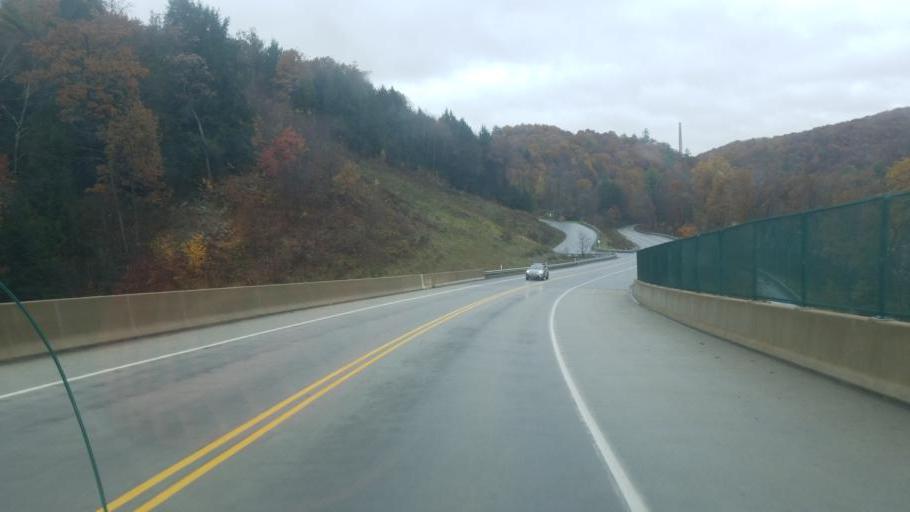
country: US
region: Pennsylvania
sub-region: Clearfield County
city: Clearfield
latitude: 41.0488
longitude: -78.3829
